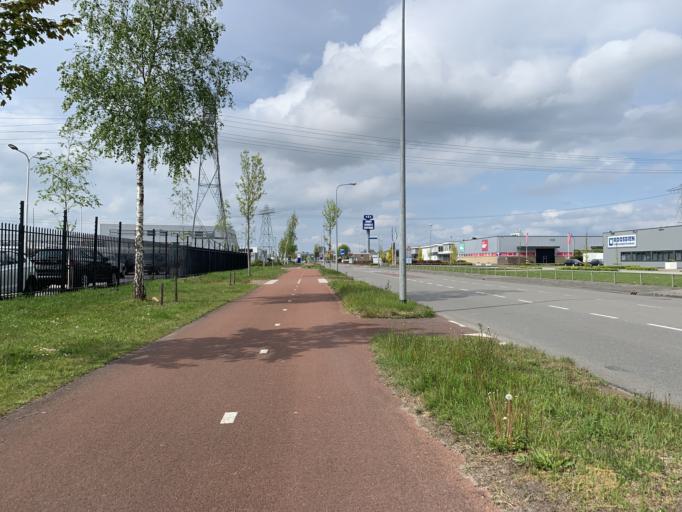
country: NL
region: Groningen
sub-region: Gemeente Groningen
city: Oosterpark
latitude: 53.2095
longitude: 6.5961
